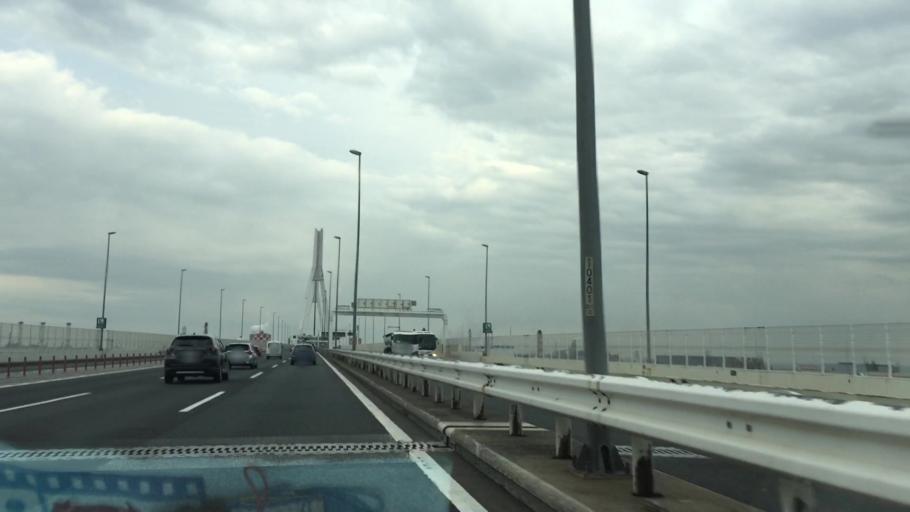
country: JP
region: Kanagawa
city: Yokohama
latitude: 35.4663
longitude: 139.6860
